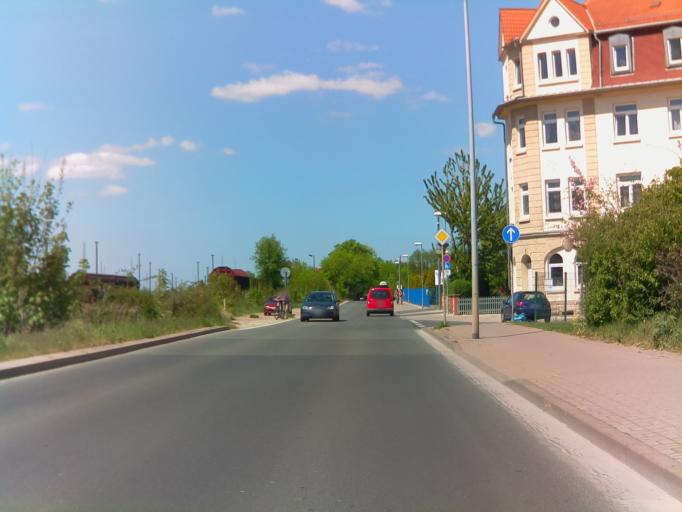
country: DE
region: Thuringia
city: Arnstadt
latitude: 50.8432
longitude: 10.9487
